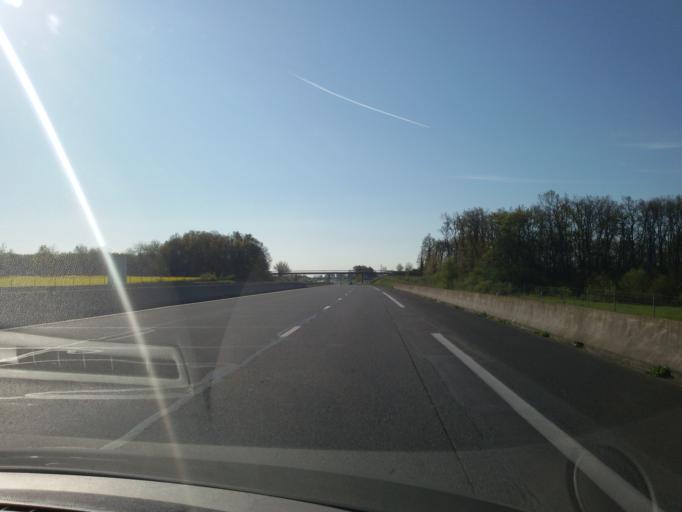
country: FR
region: Ile-de-France
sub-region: Departement de Seine-et-Marne
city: Souppes-sur-Loing
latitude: 48.2153
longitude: 2.7765
